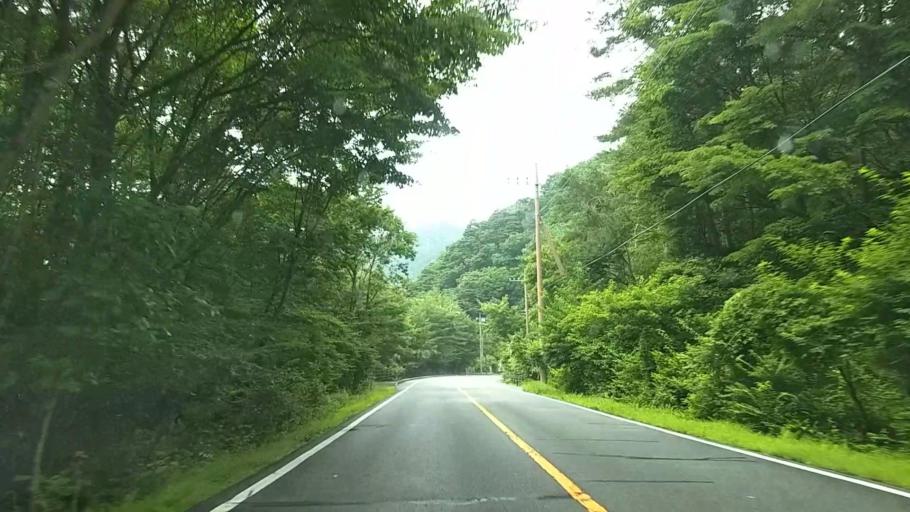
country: JP
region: Yamanashi
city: Fujikawaguchiko
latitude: 35.4706
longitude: 138.5976
